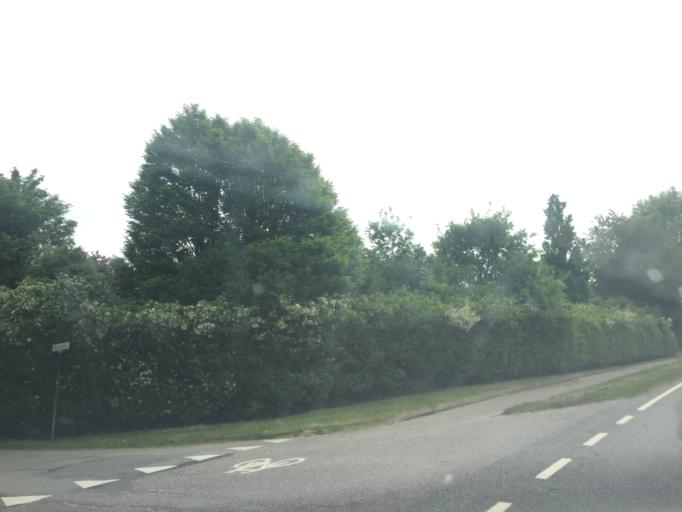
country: DK
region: South Denmark
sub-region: Kolding Kommune
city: Sonder Bjert
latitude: 55.4559
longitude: 9.5531
